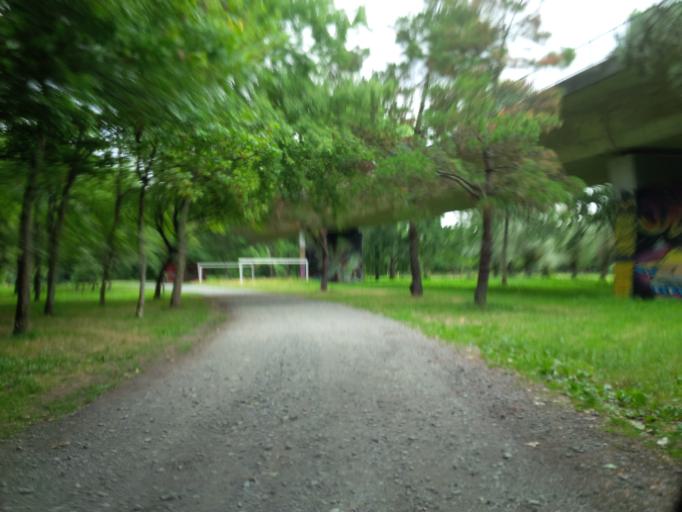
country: FR
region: Pays de la Loire
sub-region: Departement de la Loire-Atlantique
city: Reze
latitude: 47.1804
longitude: -1.5260
